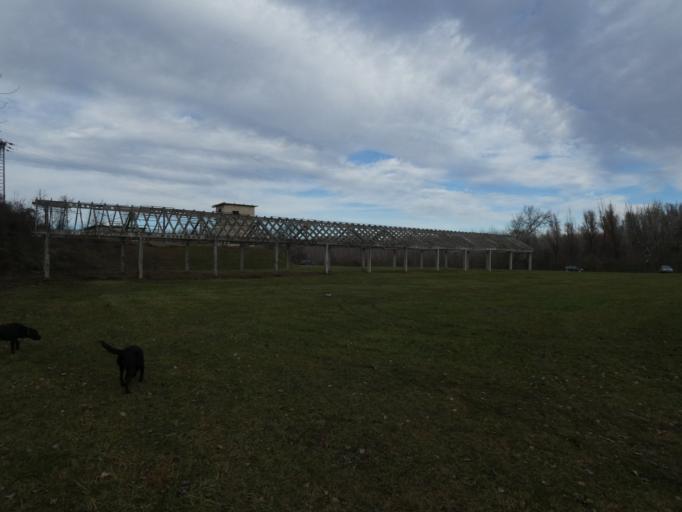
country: HU
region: Pest
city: Szazhalombatta
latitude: 47.3491
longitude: 18.9423
